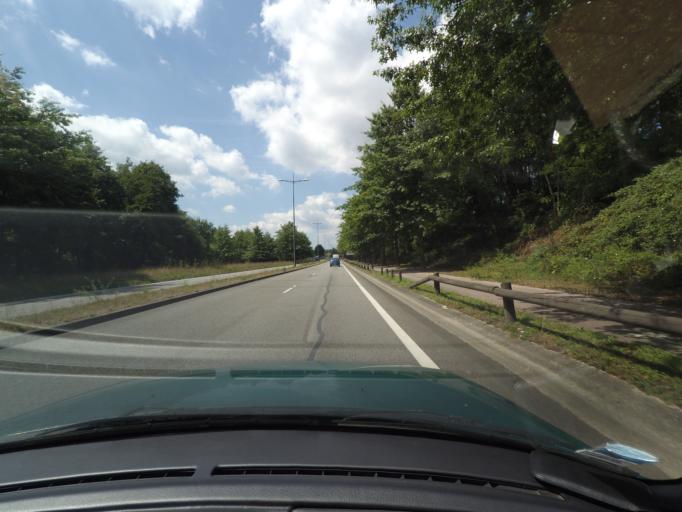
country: FR
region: Limousin
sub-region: Departement de la Haute-Vienne
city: Condat-sur-Vienne
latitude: 45.8036
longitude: 1.2837
